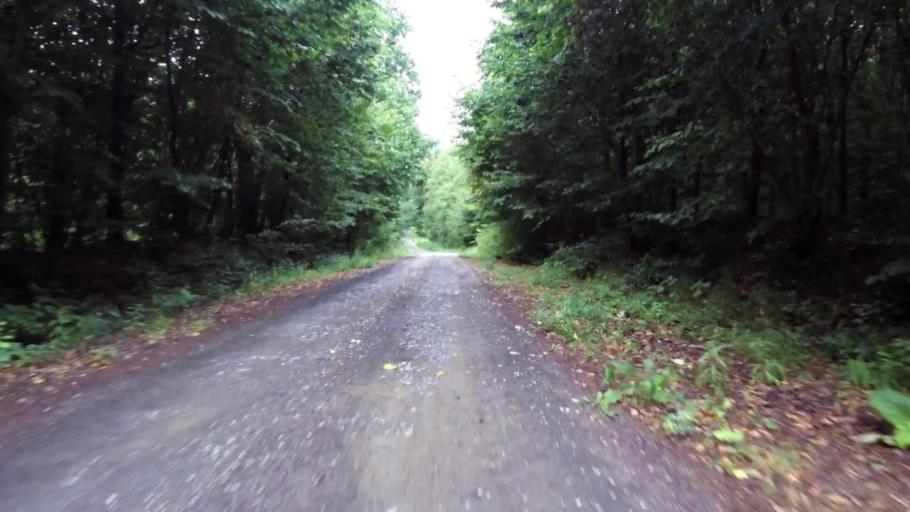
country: PL
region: West Pomeranian Voivodeship
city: Trzcinsko Zdroj
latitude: 52.8725
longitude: 14.6886
